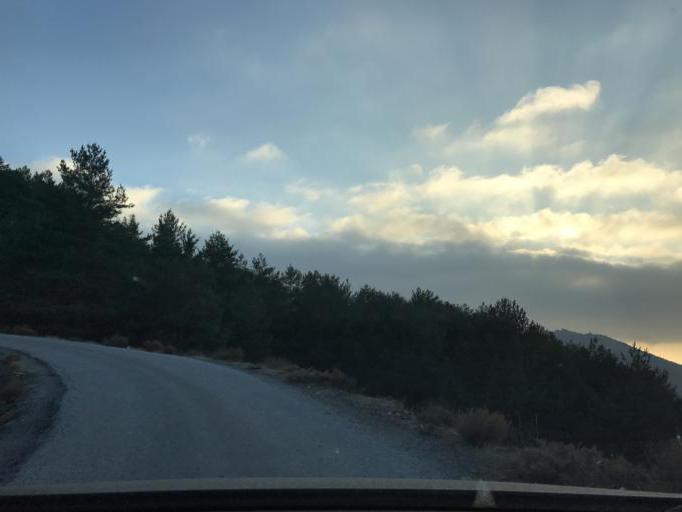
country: ES
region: Andalusia
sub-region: Provincia de Granada
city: Guejar-Sierra
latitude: 37.1371
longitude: -3.4296
